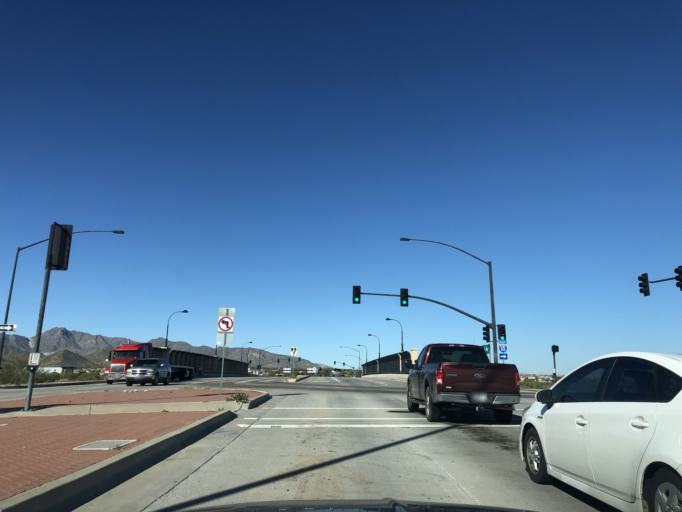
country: US
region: Arizona
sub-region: Maricopa County
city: Citrus Park
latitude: 33.4602
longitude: -112.5043
